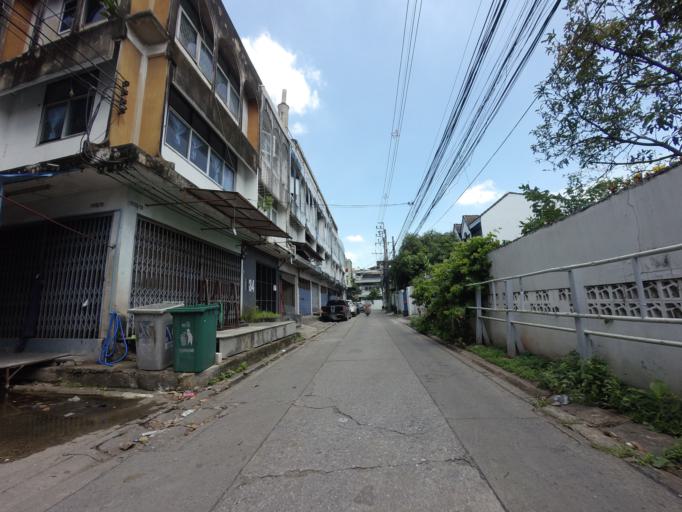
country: TH
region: Bangkok
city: Lat Phrao
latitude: 13.7998
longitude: 100.5863
